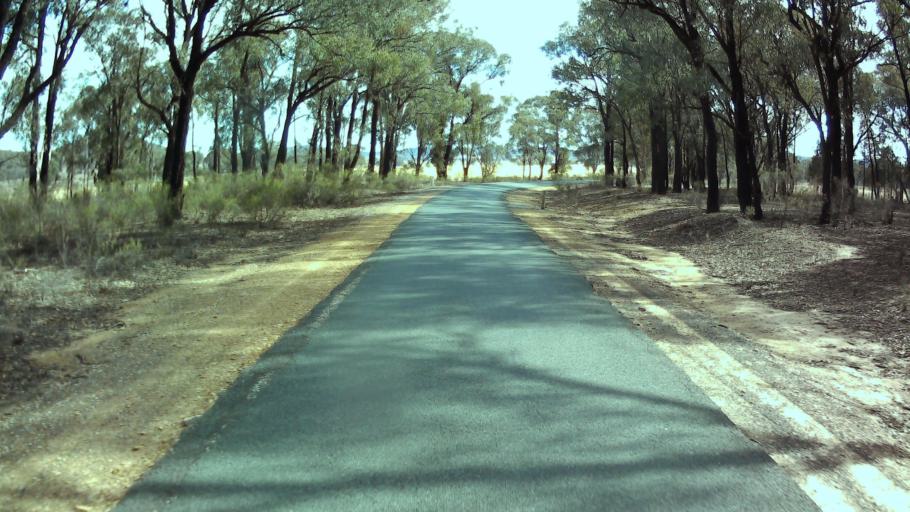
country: AU
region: New South Wales
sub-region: Weddin
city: Grenfell
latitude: -33.8545
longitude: 148.2177
